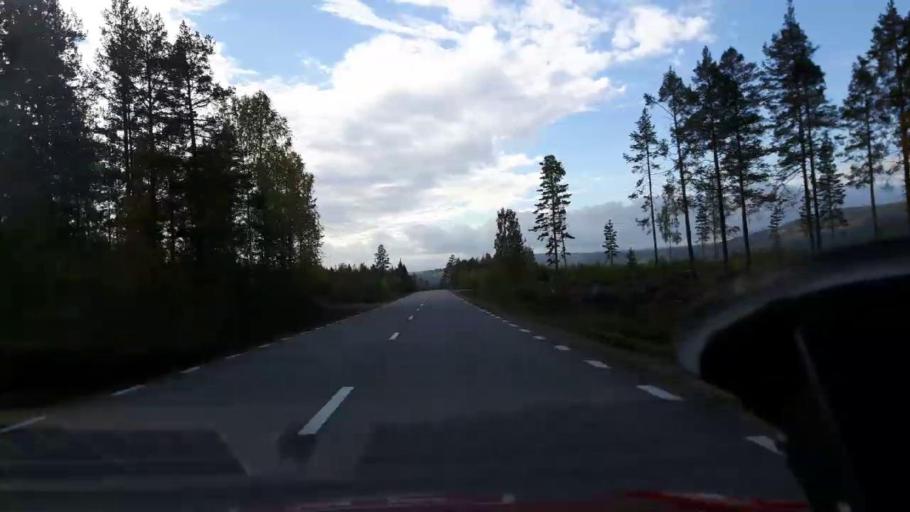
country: SE
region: Gaevleborg
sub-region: Ljusdals Kommun
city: Farila
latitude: 62.0078
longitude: 15.2404
